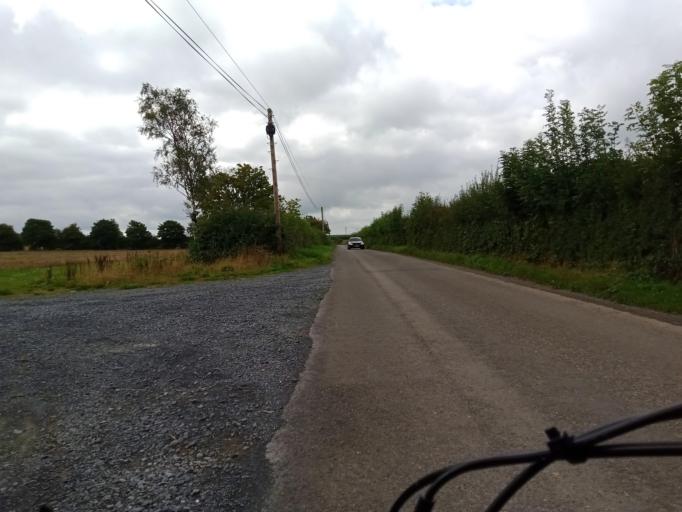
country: IE
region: Leinster
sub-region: Kilkenny
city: Callan
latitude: 52.5355
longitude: -7.2790
